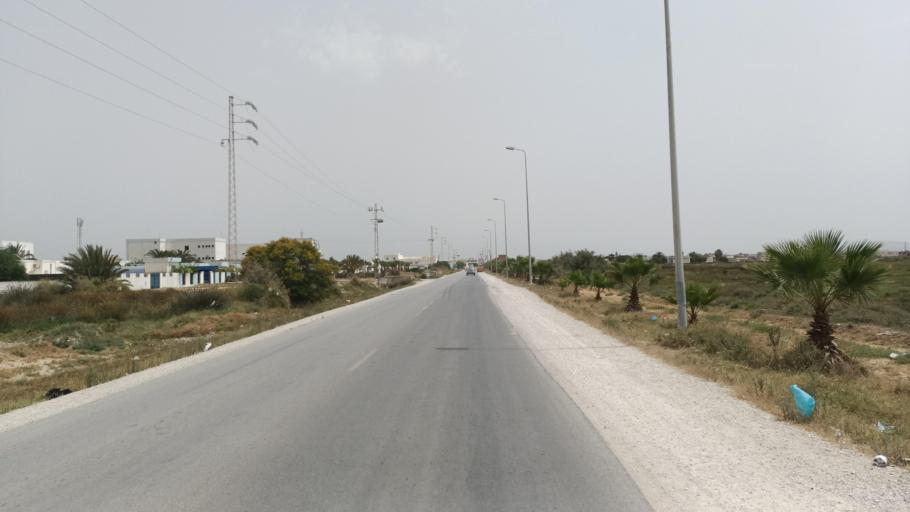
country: TN
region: Nabul
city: Manzil Bu Zalafah
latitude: 36.7136
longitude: 10.4801
